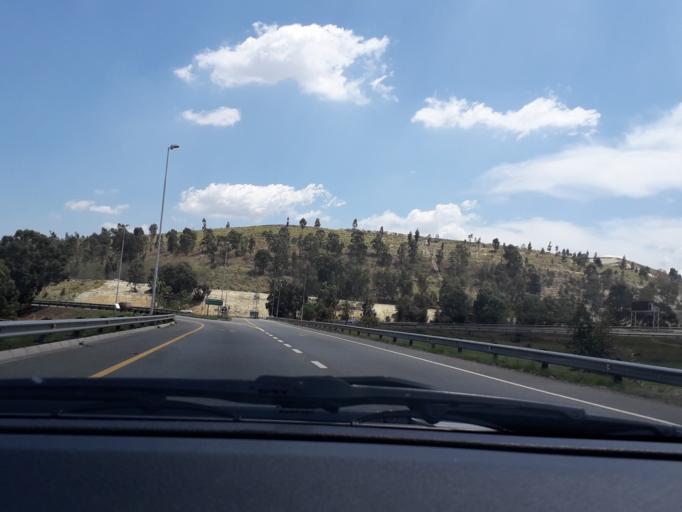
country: ZA
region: Gauteng
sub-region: City of Johannesburg Metropolitan Municipality
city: Johannesburg
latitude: -26.2345
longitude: 27.9586
